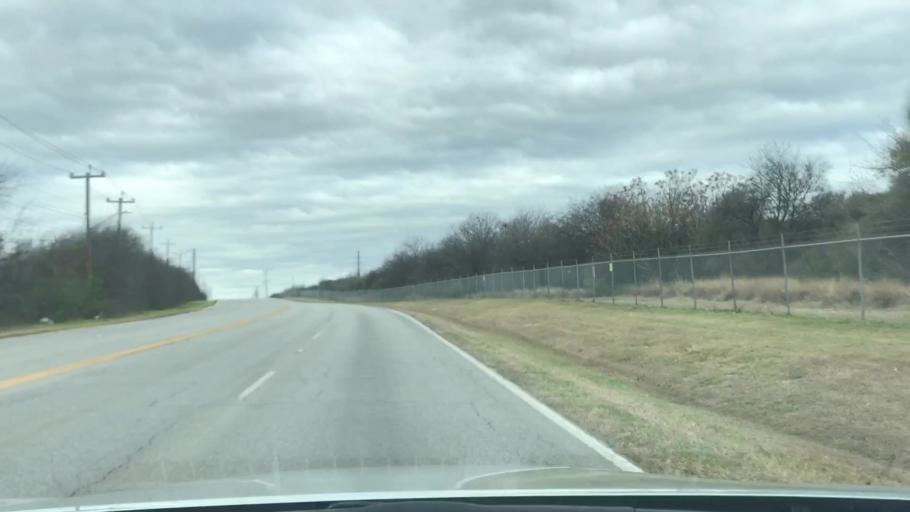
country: US
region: Texas
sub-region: Bexar County
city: Lackland Air Force Base
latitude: 29.4361
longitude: -98.6068
